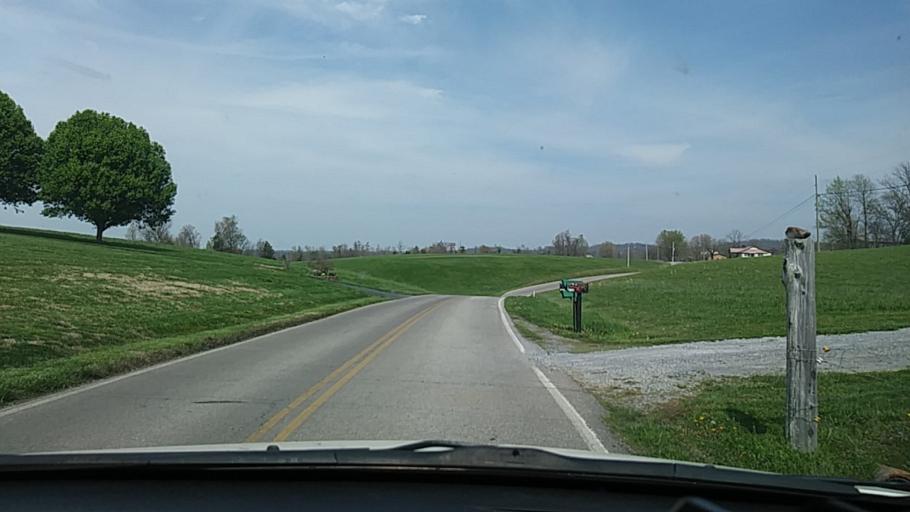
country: US
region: Tennessee
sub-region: Greene County
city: Tusculum
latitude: 36.0911
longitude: -82.7195
